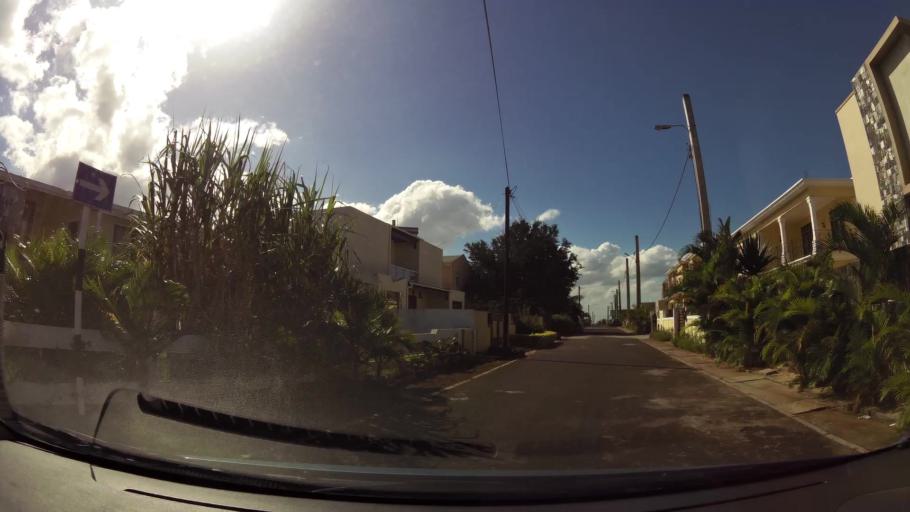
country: MU
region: Black River
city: Albion
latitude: -20.2231
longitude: 57.4130
